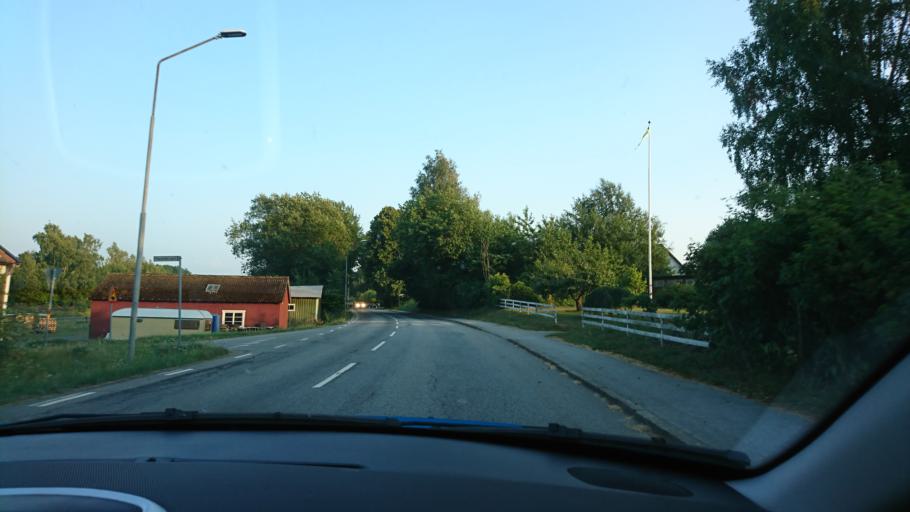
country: SE
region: Skane
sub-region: Simrishamns Kommun
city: Kivik
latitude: 55.6866
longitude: 14.1543
